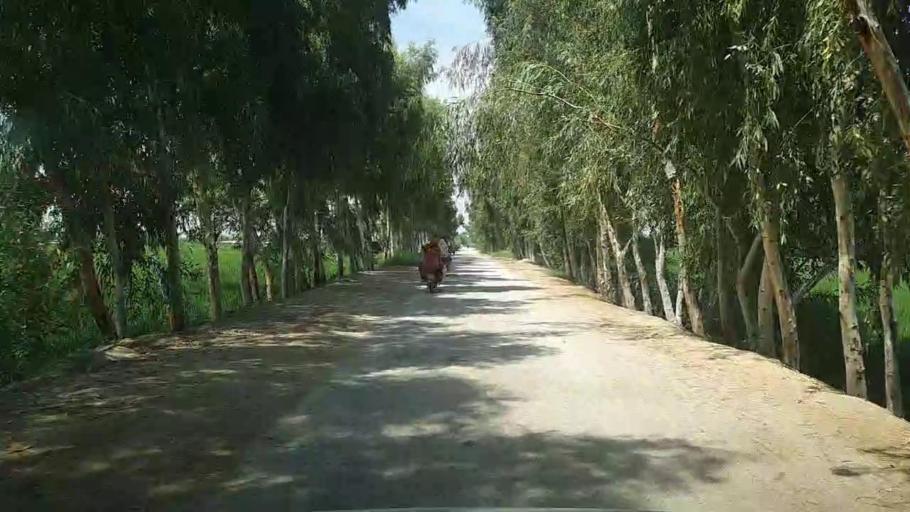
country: PK
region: Sindh
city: Kandhkot
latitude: 28.2915
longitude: 69.2383
